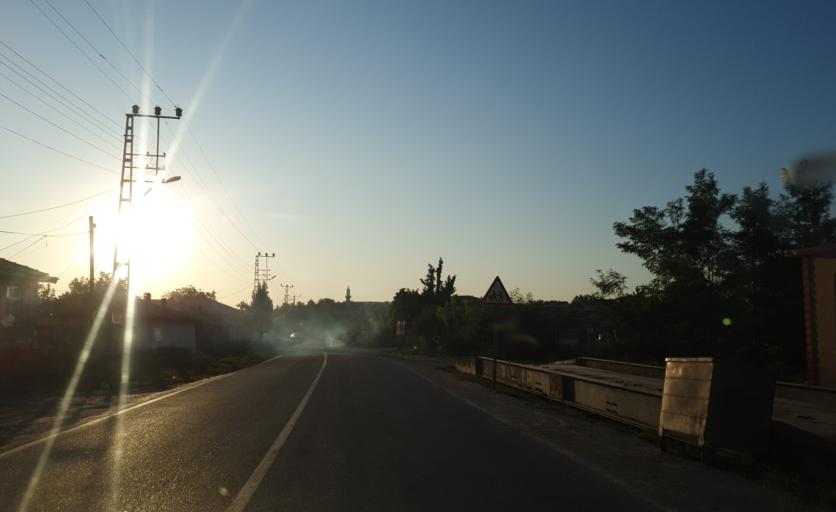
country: TR
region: Tekirdag
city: Beyazkoy
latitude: 41.3356
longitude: 27.7412
